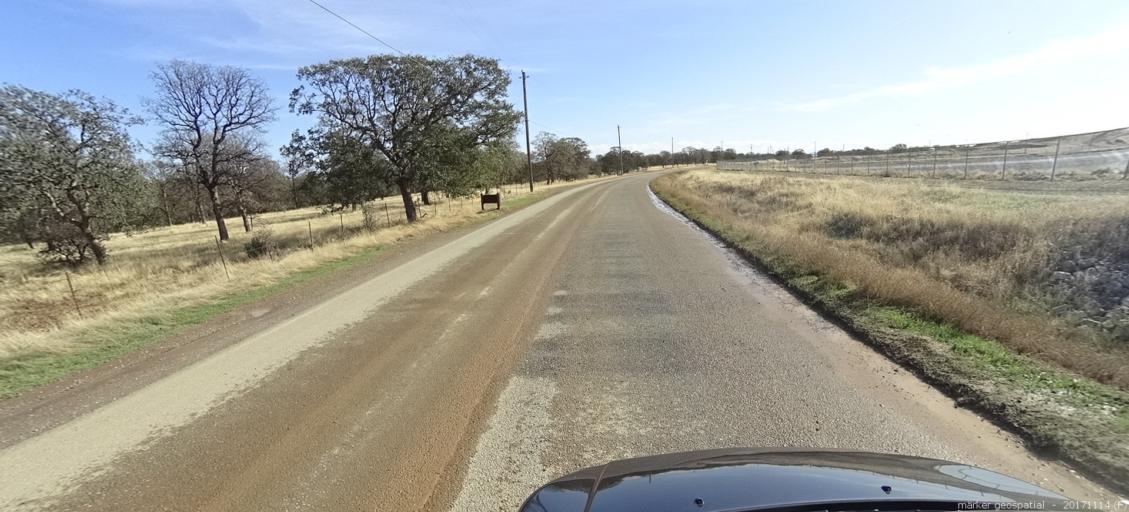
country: US
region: California
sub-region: Shasta County
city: Anderson
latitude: 40.4175
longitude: -122.3535
